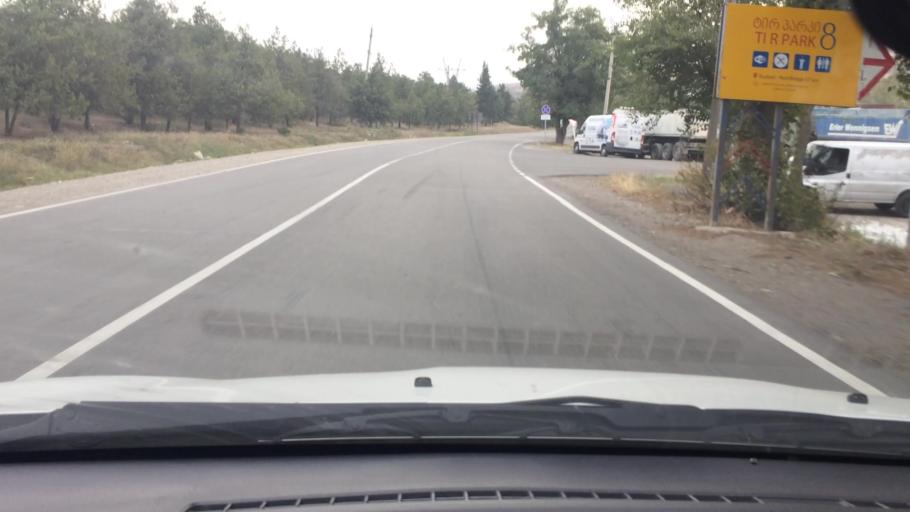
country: GE
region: Kvemo Kartli
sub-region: Gardabani
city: Gardabani
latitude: 41.3395
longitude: 45.0690
